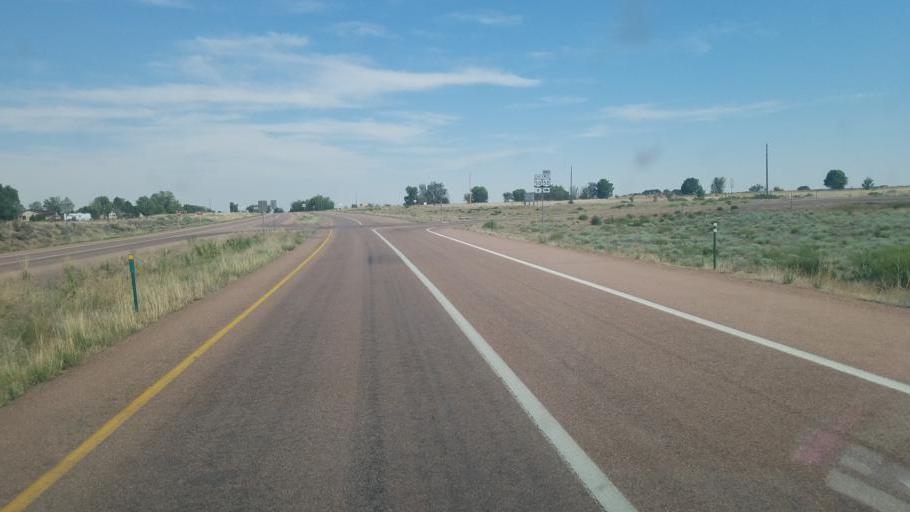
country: US
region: Colorado
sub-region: Pueblo County
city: Pueblo
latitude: 38.2347
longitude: -104.3276
